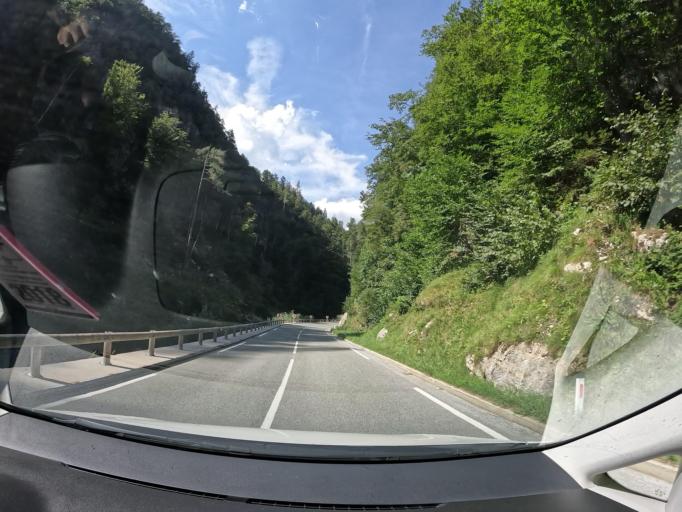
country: SI
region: Trzic
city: Trzic
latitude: 46.4013
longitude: 14.3315
